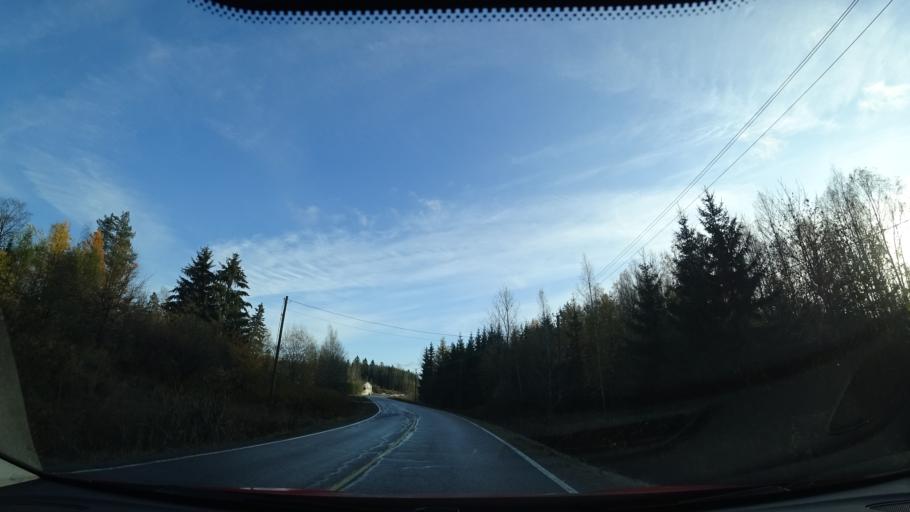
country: FI
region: Uusimaa
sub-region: Helsinki
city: Sibbo
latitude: 60.2814
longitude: 25.1961
